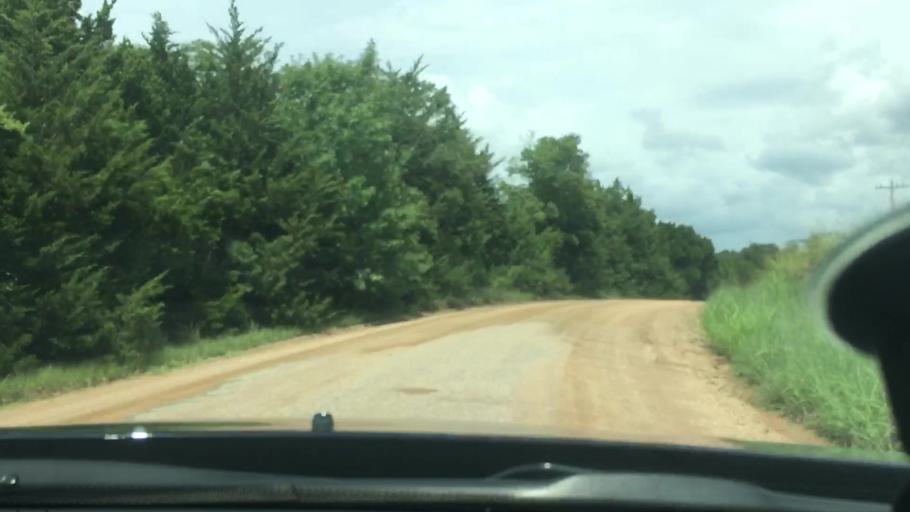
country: US
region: Oklahoma
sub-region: Carter County
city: Dickson
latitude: 34.2460
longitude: -96.9286
